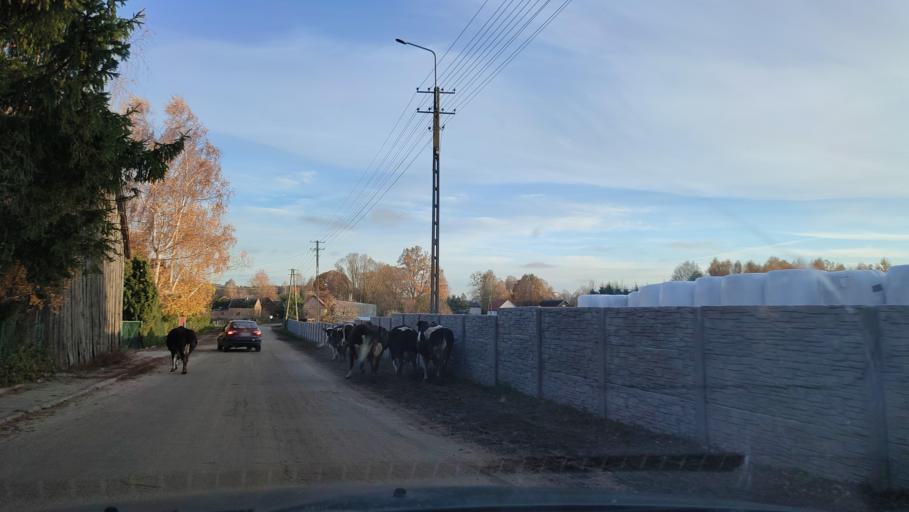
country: PL
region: Masovian Voivodeship
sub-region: Powiat mlawski
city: Dzierzgowo
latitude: 53.2784
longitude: 20.6466
